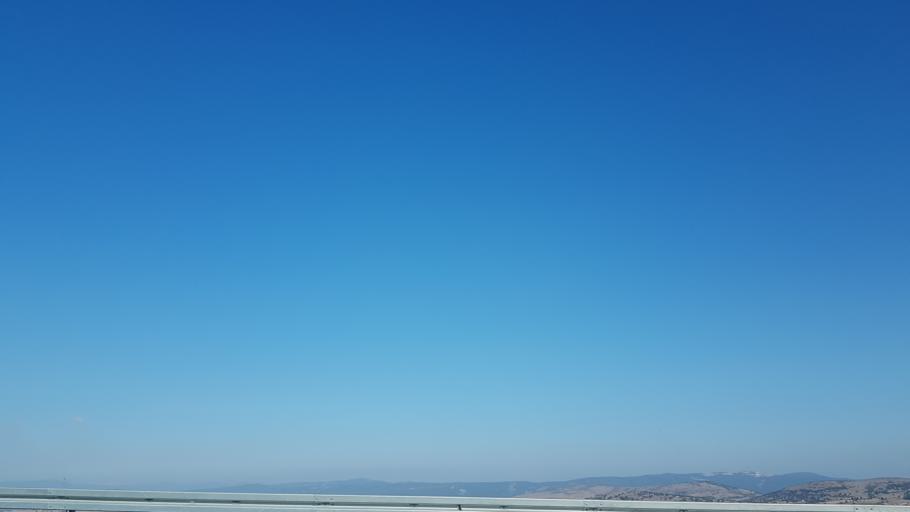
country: TR
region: Balikesir
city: Ertugrul
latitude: 39.6330
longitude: 27.7094
